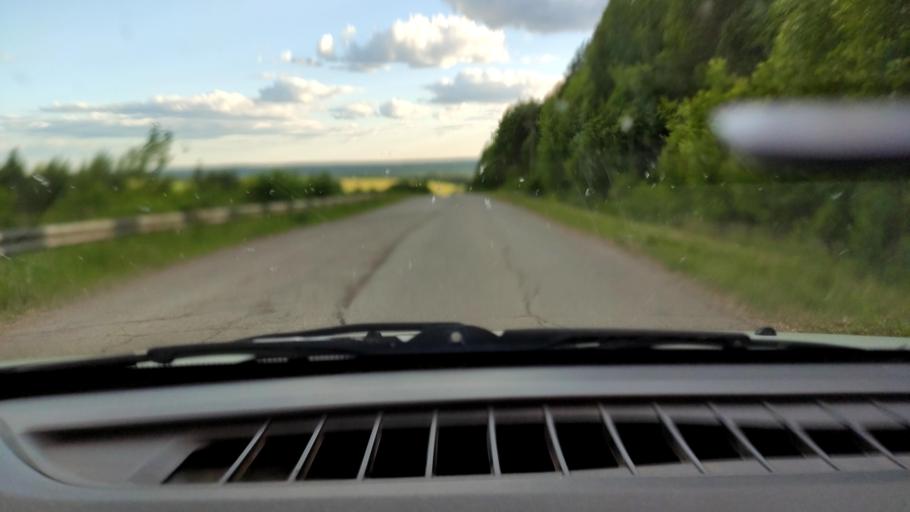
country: RU
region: Perm
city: Uinskoye
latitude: 57.0820
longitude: 56.6162
